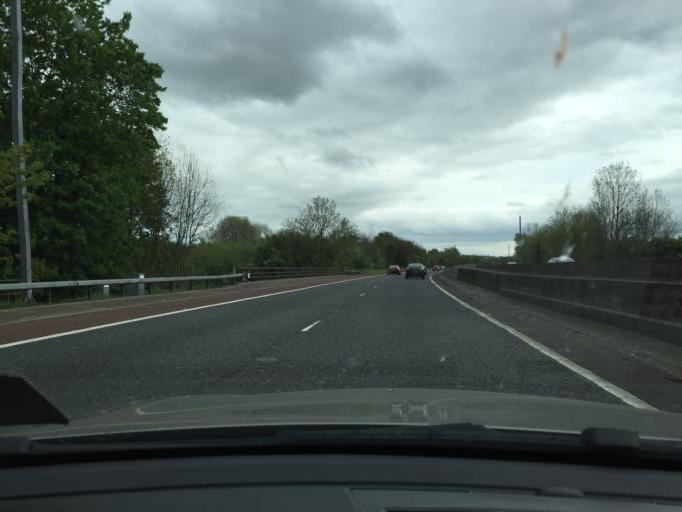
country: GB
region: Northern Ireland
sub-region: Lisburn District
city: Lisburn
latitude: 54.5438
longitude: -5.9937
